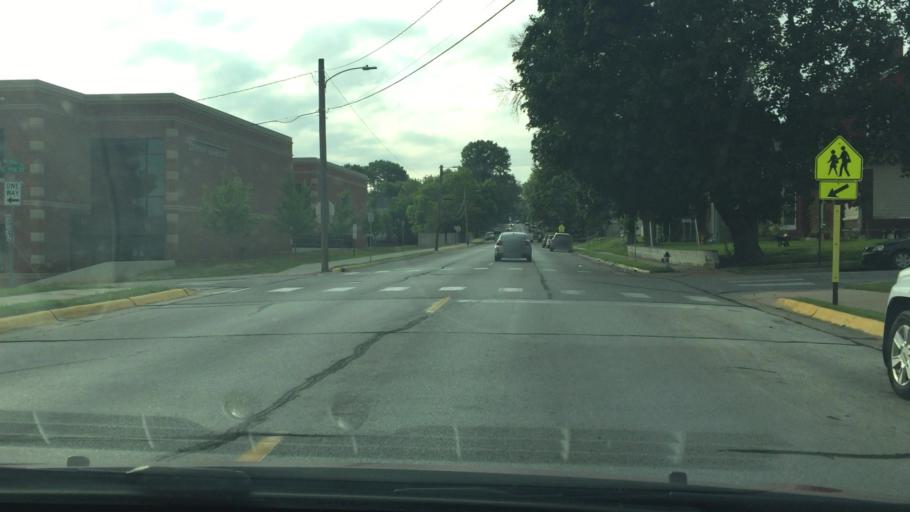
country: US
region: Iowa
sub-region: Muscatine County
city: Muscatine
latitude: 41.4291
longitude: -91.0468
